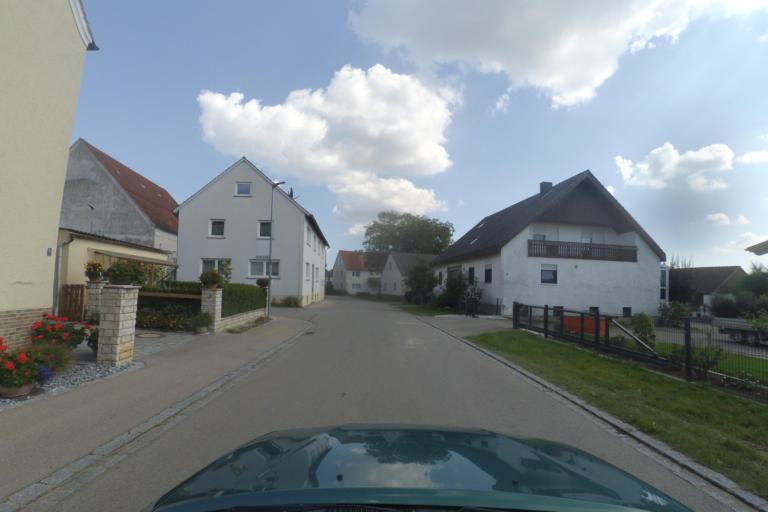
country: DE
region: Bavaria
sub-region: Swabia
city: Maihingen
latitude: 48.9611
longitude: 10.5321
